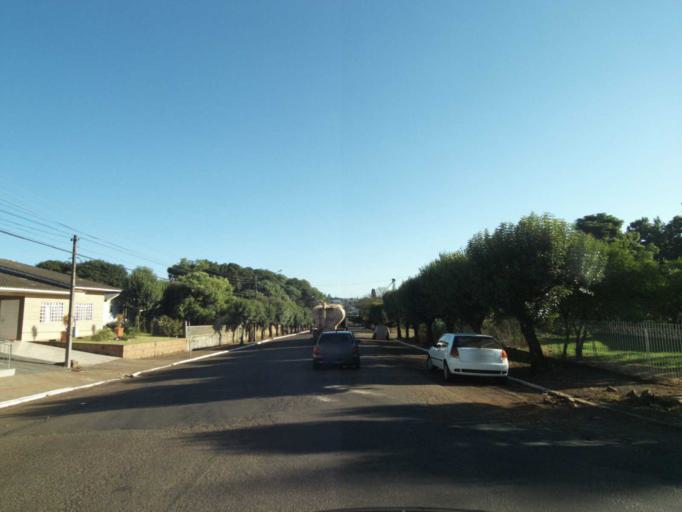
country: BR
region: Parana
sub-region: Coronel Vivida
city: Coronel Vivida
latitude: -25.9612
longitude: -52.8141
